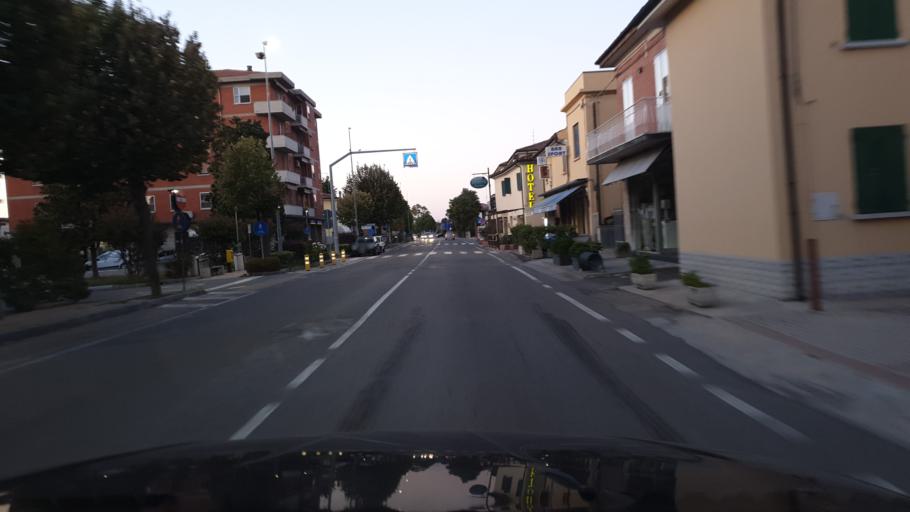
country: IT
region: Emilia-Romagna
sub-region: Provincia di Bologna
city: Altedo
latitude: 44.6671
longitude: 11.4883
